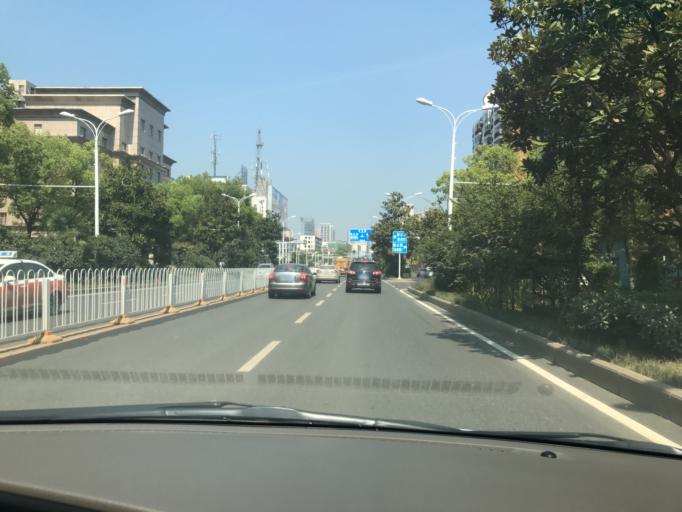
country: CN
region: Hubei
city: Shilipu
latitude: 30.5611
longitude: 114.2167
